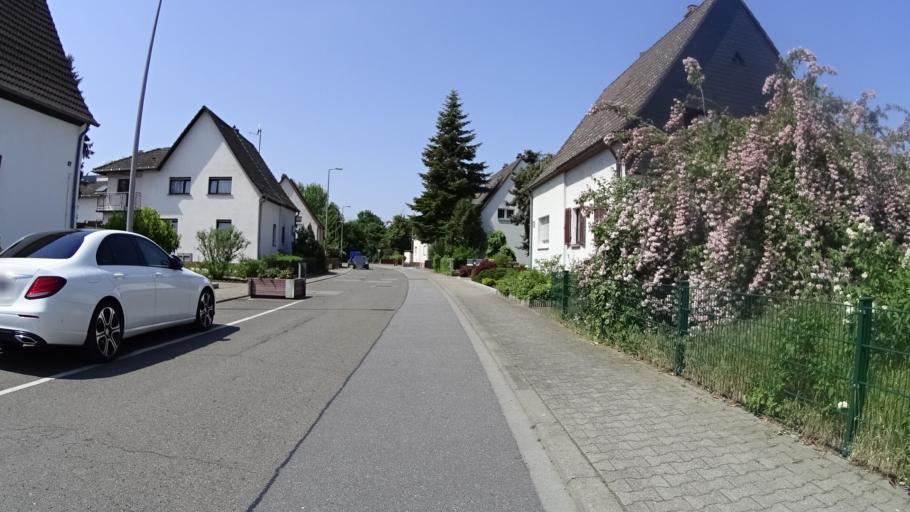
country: DE
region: Baden-Wuerttemberg
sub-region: Karlsruhe Region
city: Bruhl
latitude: 49.4202
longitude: 8.5273
